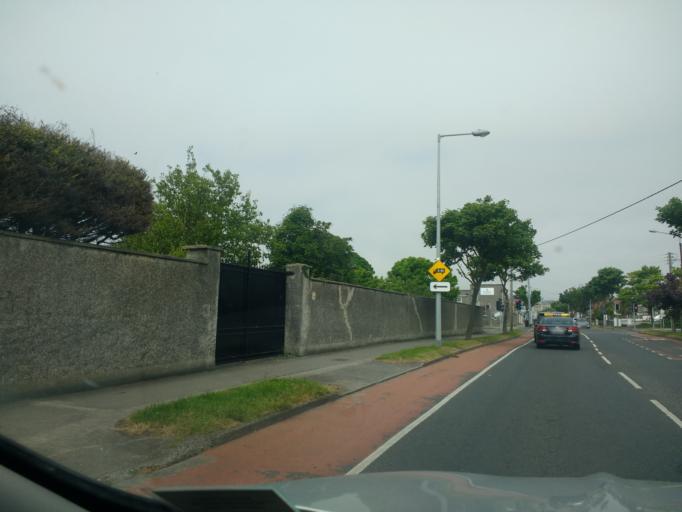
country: IE
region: Leinster
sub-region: Fingal County
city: Baldoyle
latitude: 53.3959
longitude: -6.1262
